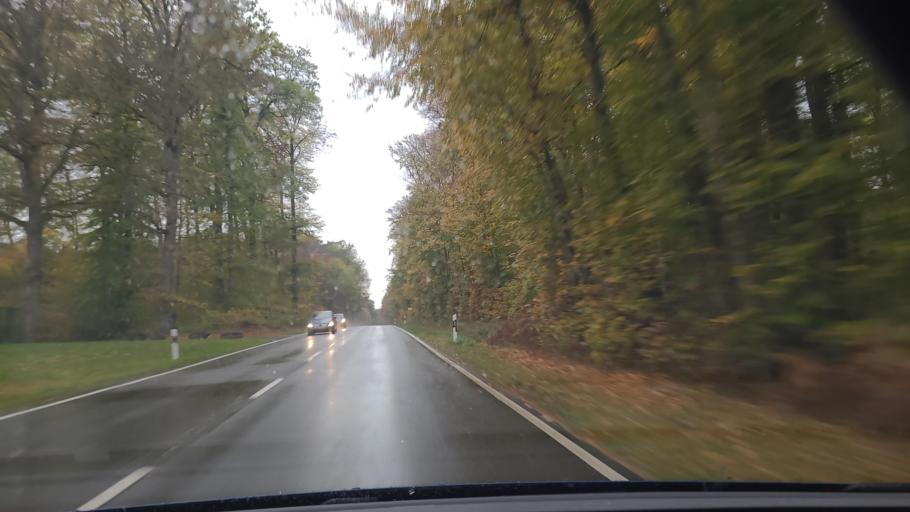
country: LU
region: Luxembourg
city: Bereldange
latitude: 49.6389
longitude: 6.1062
